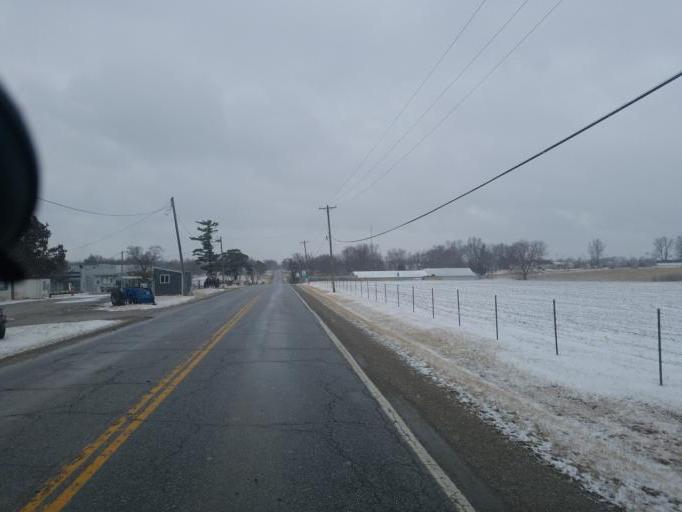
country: US
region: Missouri
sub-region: Putnam County
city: Unionville
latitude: 40.4879
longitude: -93.0092
